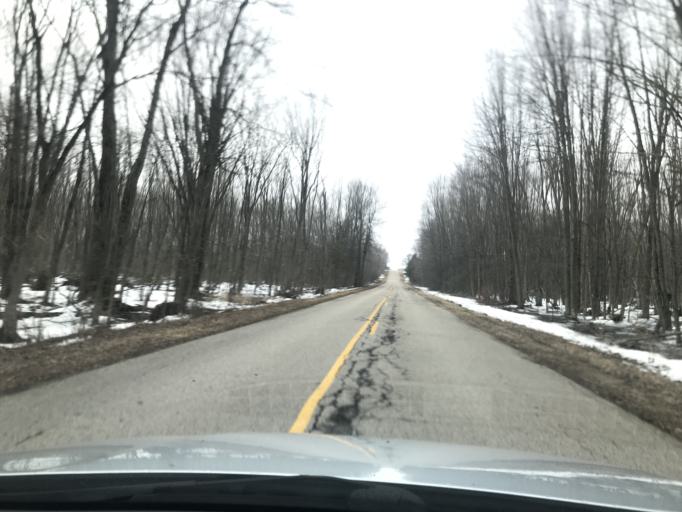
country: US
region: Wisconsin
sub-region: Oconto County
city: Oconto Falls
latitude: 44.8351
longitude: -88.1680
